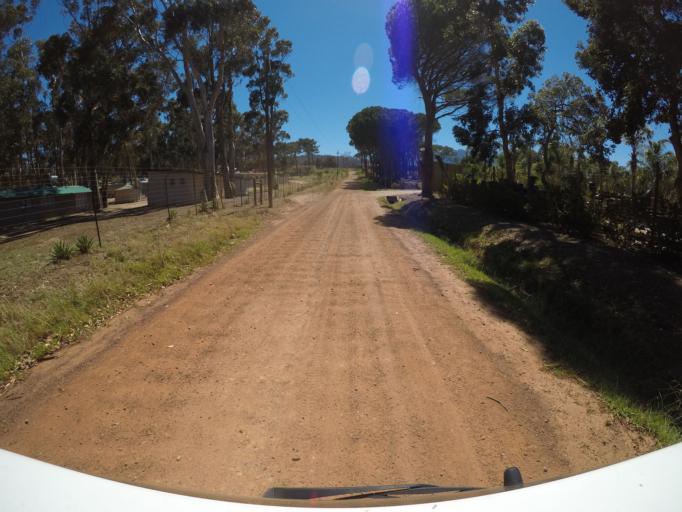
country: ZA
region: Western Cape
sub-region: Overberg District Municipality
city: Grabouw
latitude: -34.1163
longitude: 18.8780
